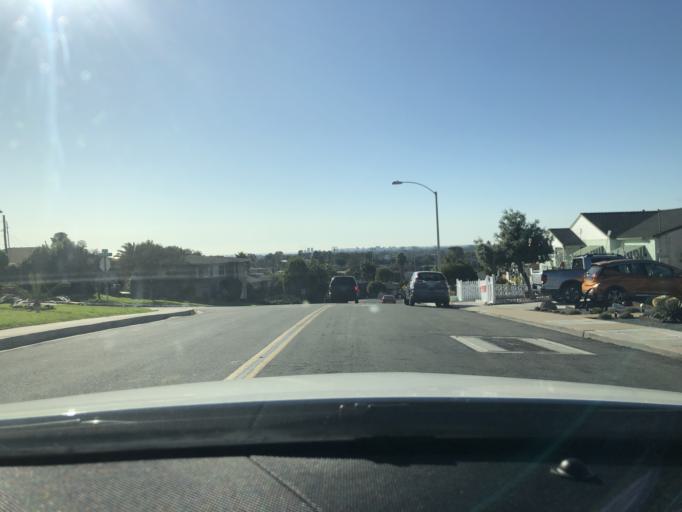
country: US
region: California
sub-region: San Diego County
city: Lemon Grove
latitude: 32.7555
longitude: -117.0714
